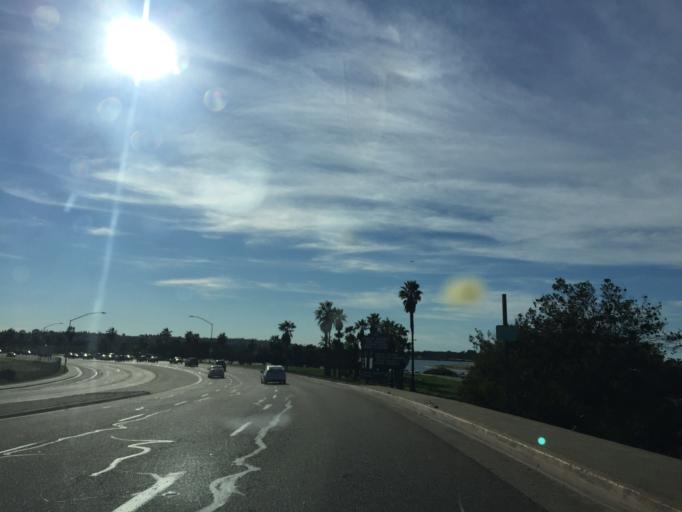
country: US
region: California
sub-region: San Diego County
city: San Diego
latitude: 32.7696
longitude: -117.2075
